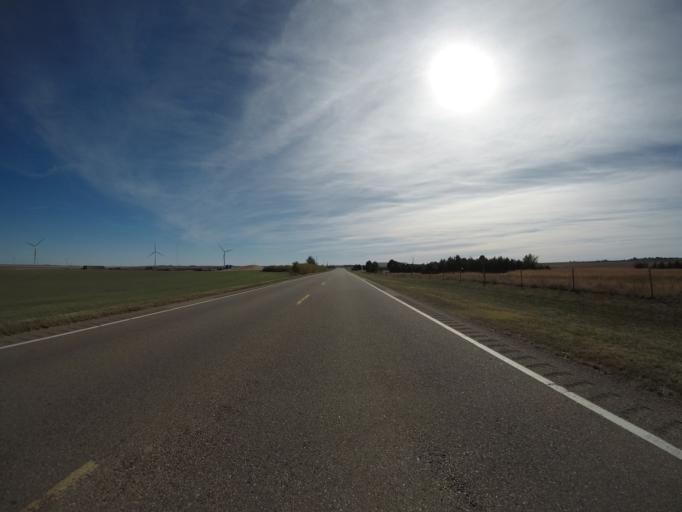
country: US
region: Colorado
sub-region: Kit Carson County
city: Burlington
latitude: 39.3547
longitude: -102.2598
